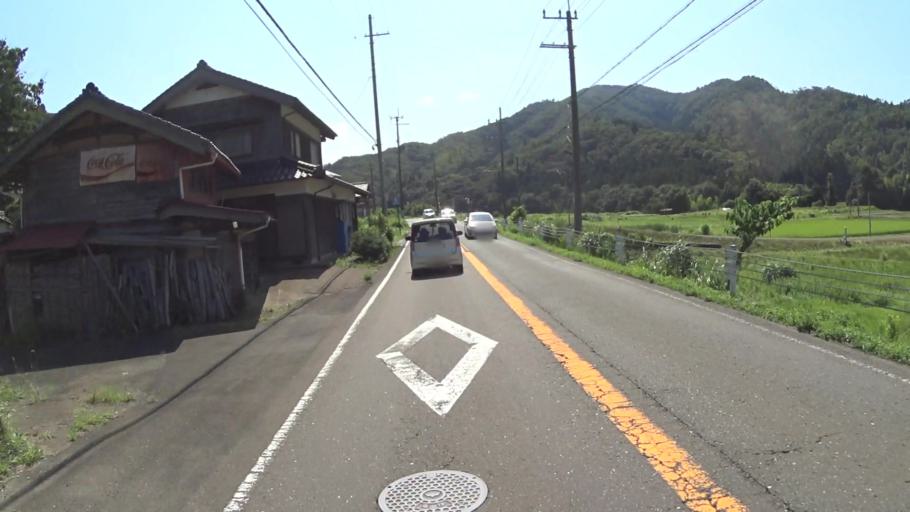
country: JP
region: Fukui
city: Obama
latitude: 35.4465
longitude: 135.7024
